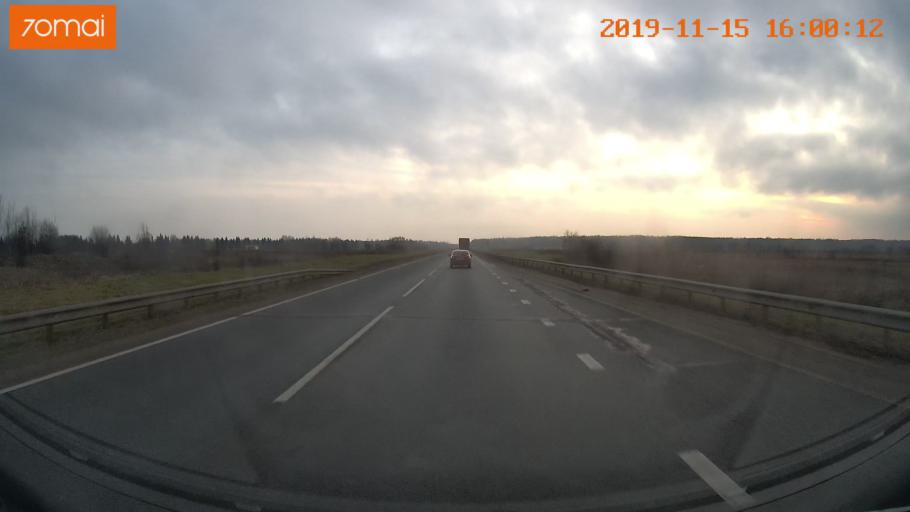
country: RU
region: Jaroslavl
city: Yaroslavl
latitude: 57.7995
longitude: 39.9407
